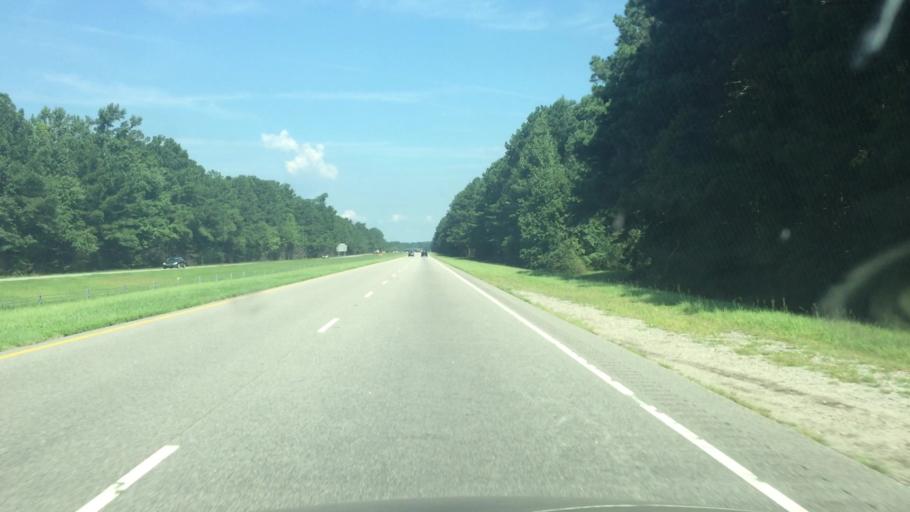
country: US
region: North Carolina
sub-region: Robeson County
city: Maxton
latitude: 34.7302
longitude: -79.3197
